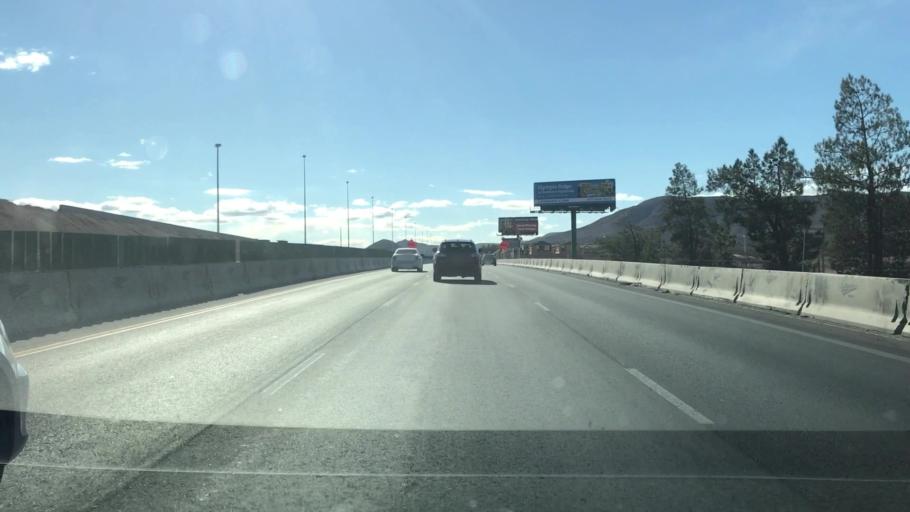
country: US
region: Nevada
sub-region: Clark County
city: Enterprise
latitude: 35.9820
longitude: -115.1816
